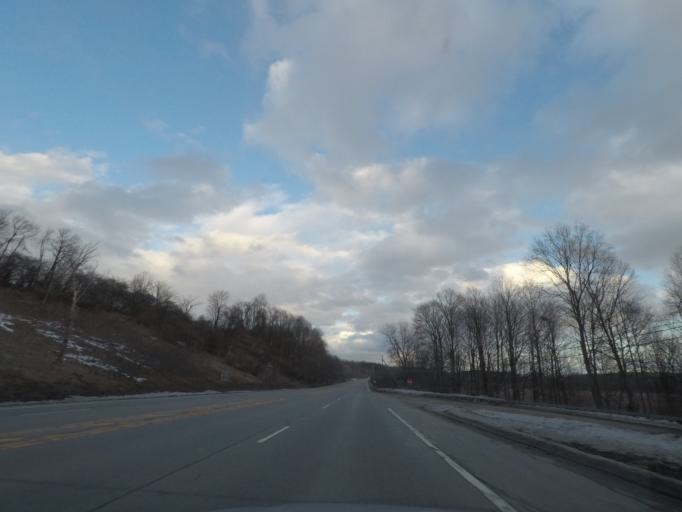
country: US
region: New York
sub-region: Herkimer County
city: Little Falls
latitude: 43.0356
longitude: -74.8142
